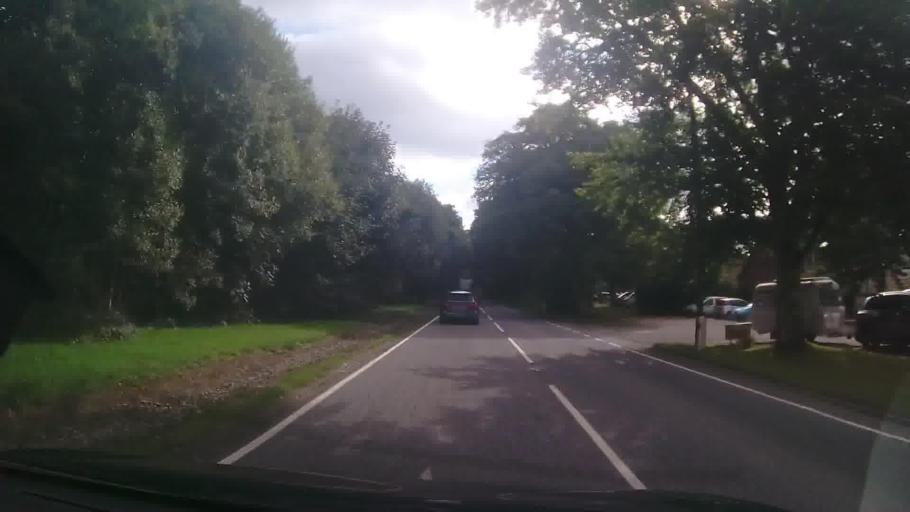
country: GB
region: Scotland
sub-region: Argyll and Bute
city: Oban
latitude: 56.4774
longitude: -5.3985
